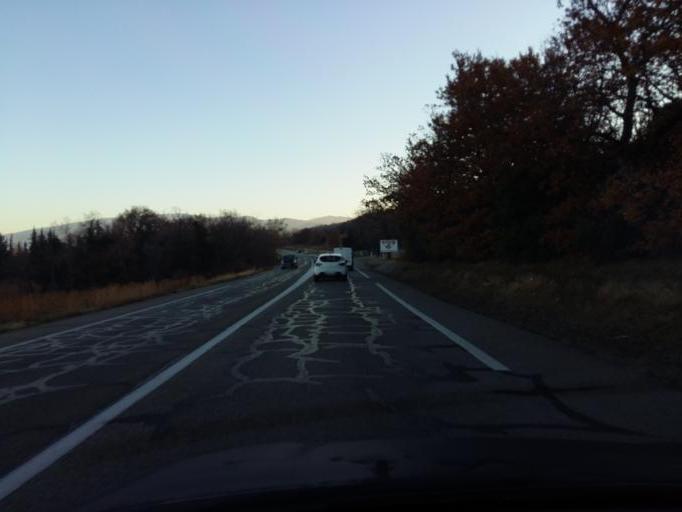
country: FR
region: Provence-Alpes-Cote d'Azur
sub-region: Departement du Vaucluse
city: Visan
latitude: 44.3500
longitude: 4.9587
